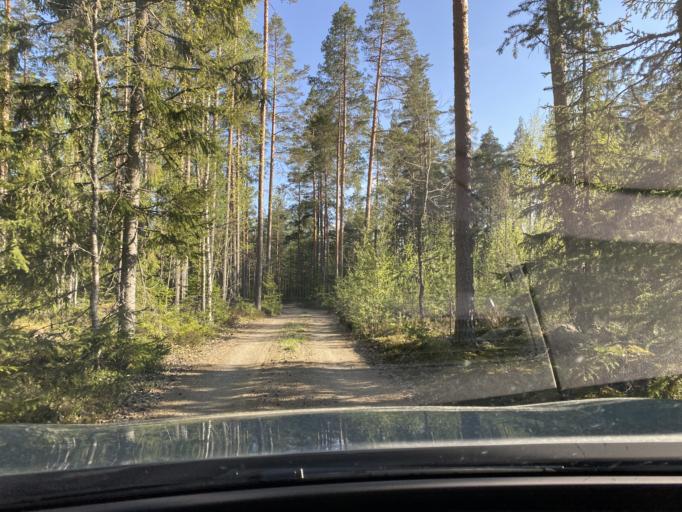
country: FI
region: Pirkanmaa
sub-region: Lounais-Pirkanmaa
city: Punkalaidun
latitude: 61.0126
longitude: 23.2038
